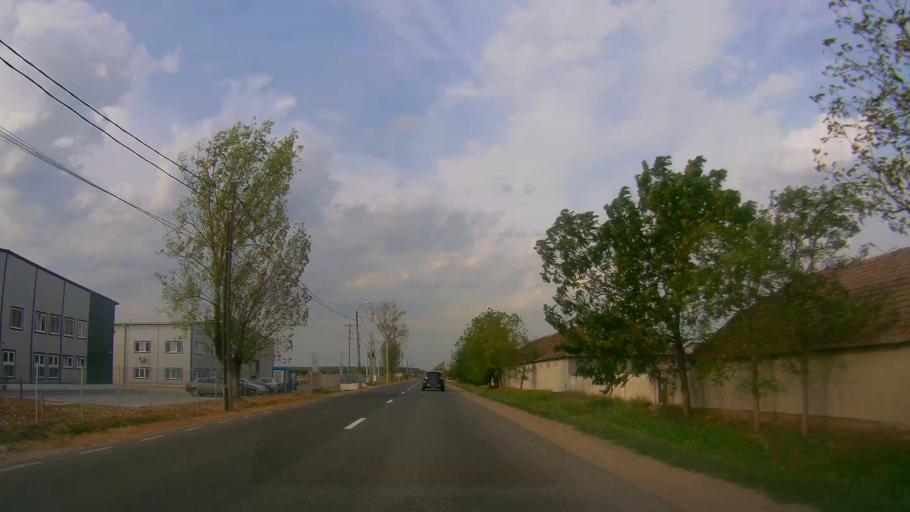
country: RO
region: Satu Mare
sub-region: Oras Ardud
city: Ardud
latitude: 47.6263
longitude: 22.8743
